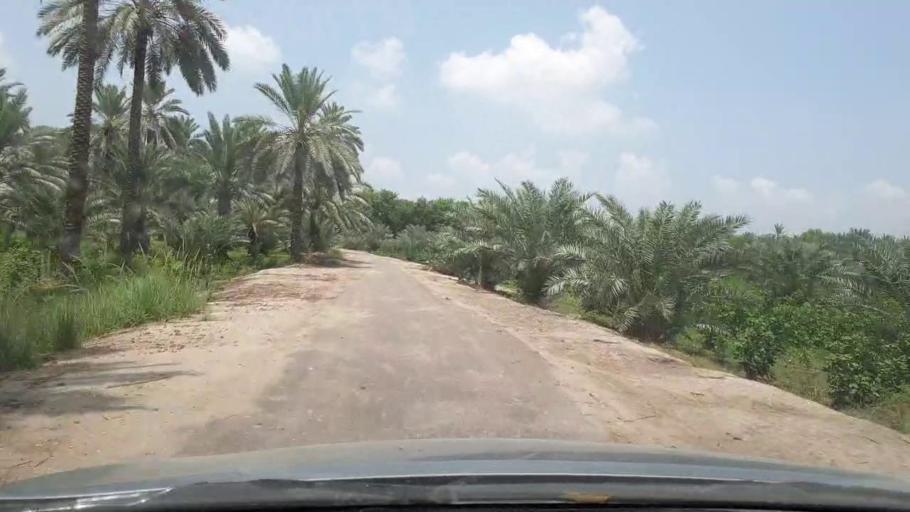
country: PK
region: Sindh
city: Khairpur
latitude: 27.4751
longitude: 68.7303
